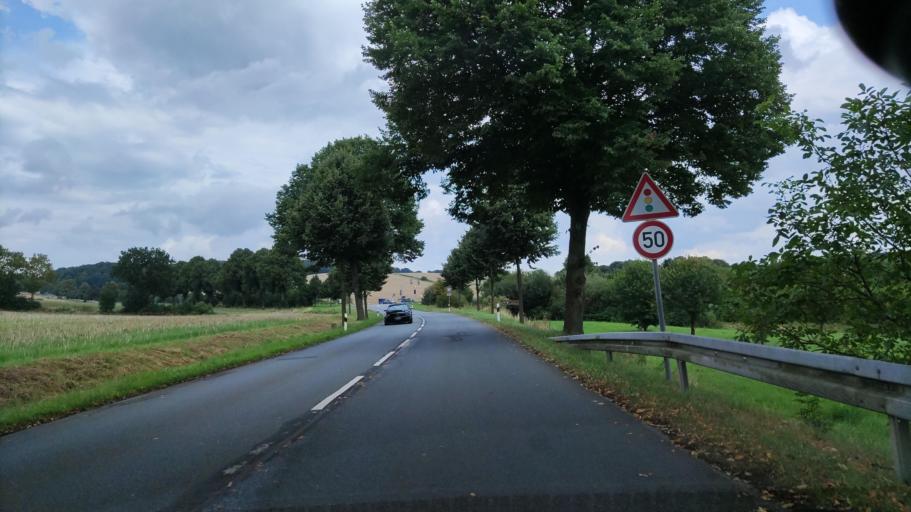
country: DE
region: Lower Saxony
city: Bevern
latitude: 51.8667
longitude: 9.5294
